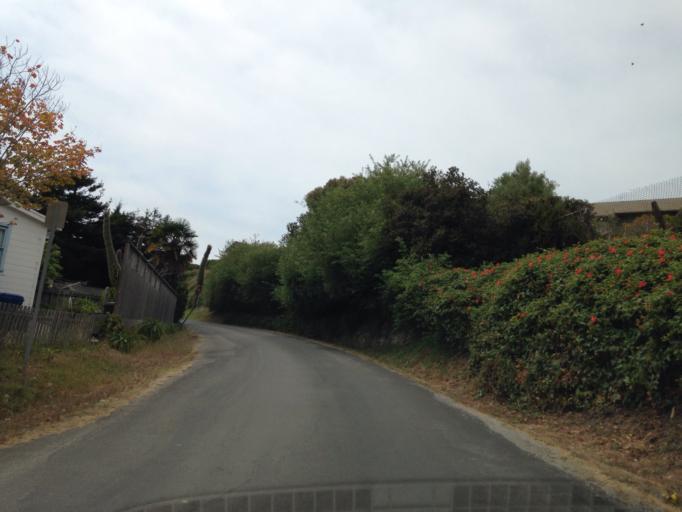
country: US
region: California
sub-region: Santa Cruz County
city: Bonny Doon
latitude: 37.0116
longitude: -122.1918
